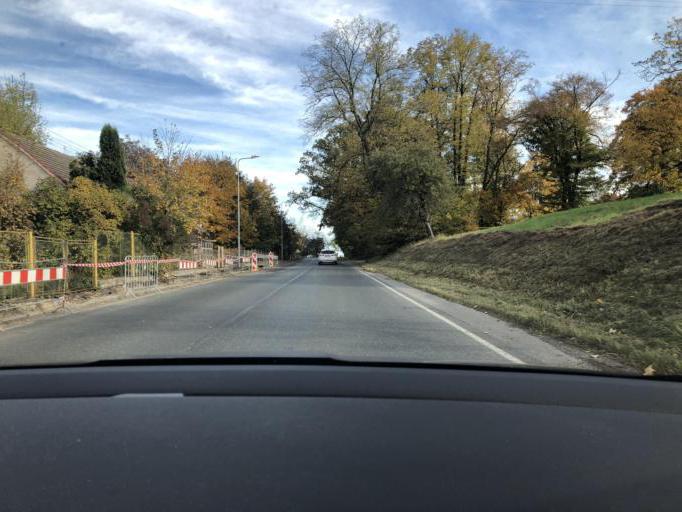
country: CZ
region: Central Bohemia
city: Divisov
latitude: 49.8037
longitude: 14.9113
